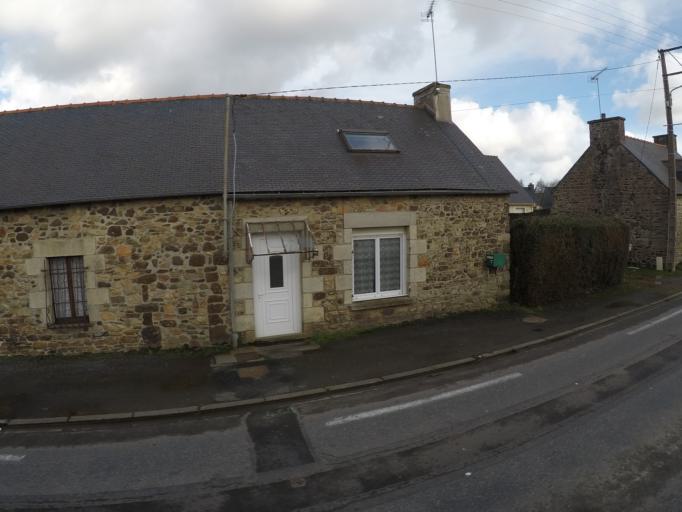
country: FR
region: Brittany
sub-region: Departement des Cotes-d'Armor
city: Lanvollon
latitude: 48.6350
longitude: -2.9904
